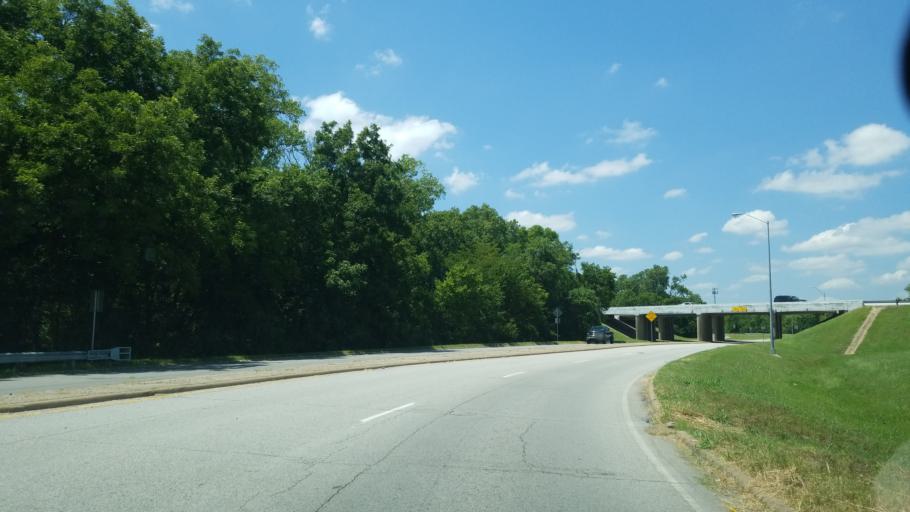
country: US
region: Texas
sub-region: Dallas County
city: Dallas
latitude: 32.7439
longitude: -96.7267
